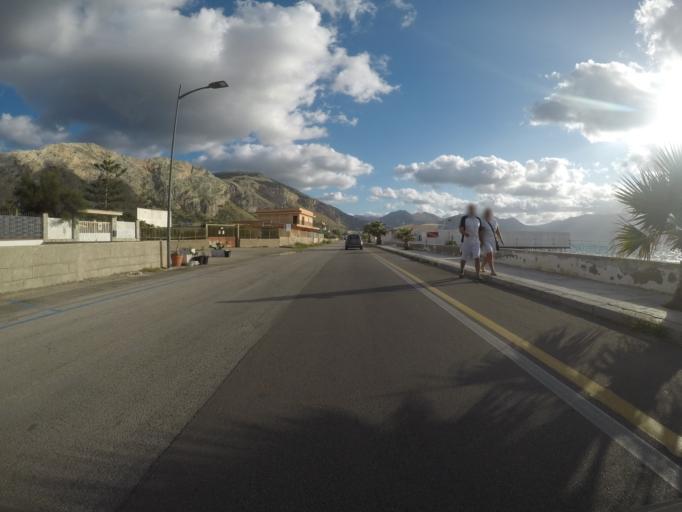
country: IT
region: Sicily
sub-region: Palermo
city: Isola delle Femmine
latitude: 38.1977
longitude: 13.2437
